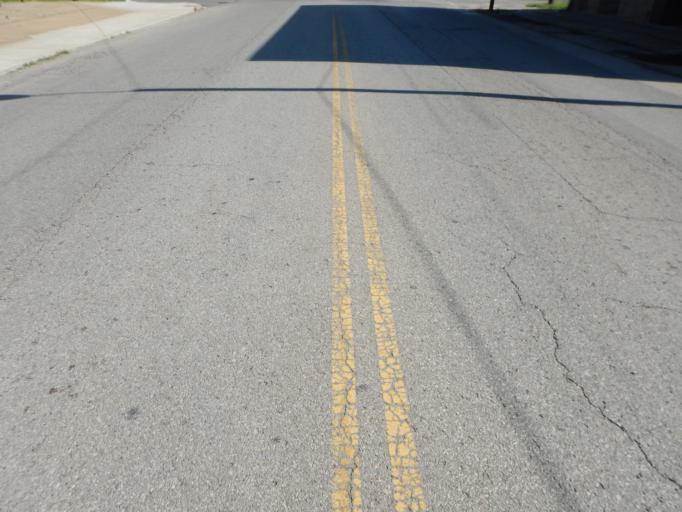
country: US
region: Ohio
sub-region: Muskingum County
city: Zanesville
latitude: 39.9245
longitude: -82.0068
